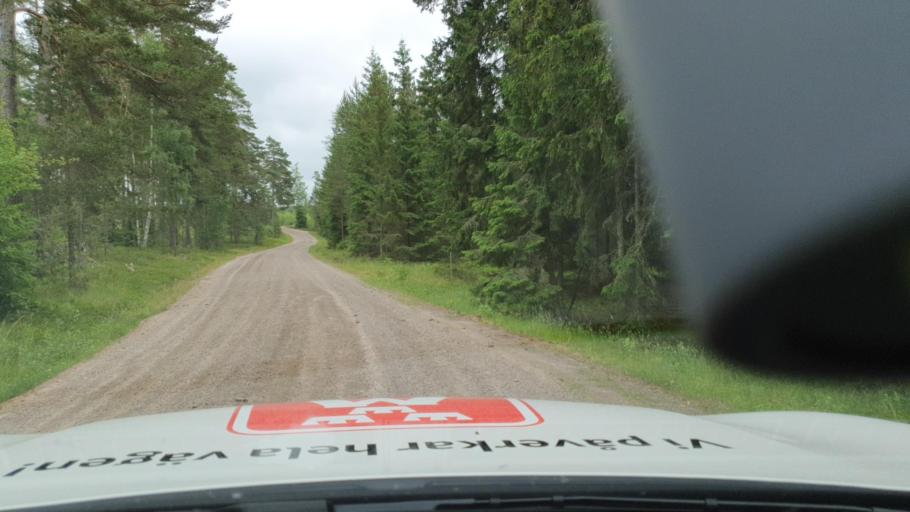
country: SE
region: Vaestra Goetaland
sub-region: Hjo Kommun
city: Hjo
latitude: 58.4072
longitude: 14.3132
